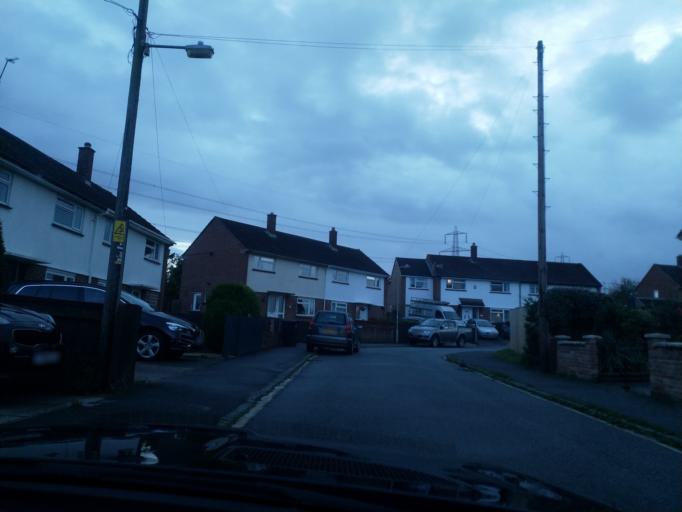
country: GB
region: England
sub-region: Oxfordshire
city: Wheatley
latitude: 51.7427
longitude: -1.1264
